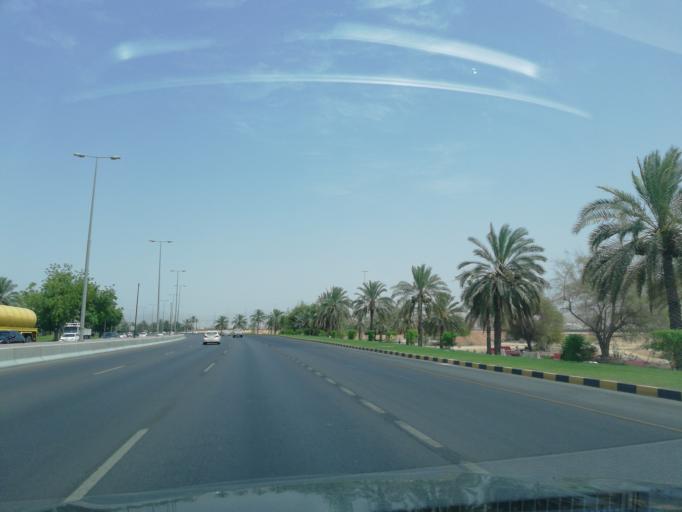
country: OM
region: Muhafazat Masqat
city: As Sib al Jadidah
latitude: 23.5836
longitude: 58.2616
